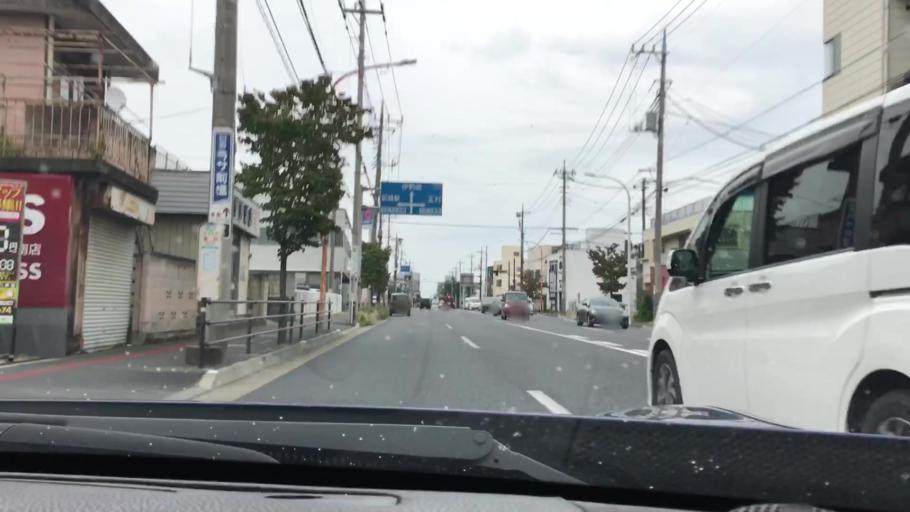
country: JP
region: Gunma
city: Maebashi-shi
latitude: 36.3762
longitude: 139.0690
